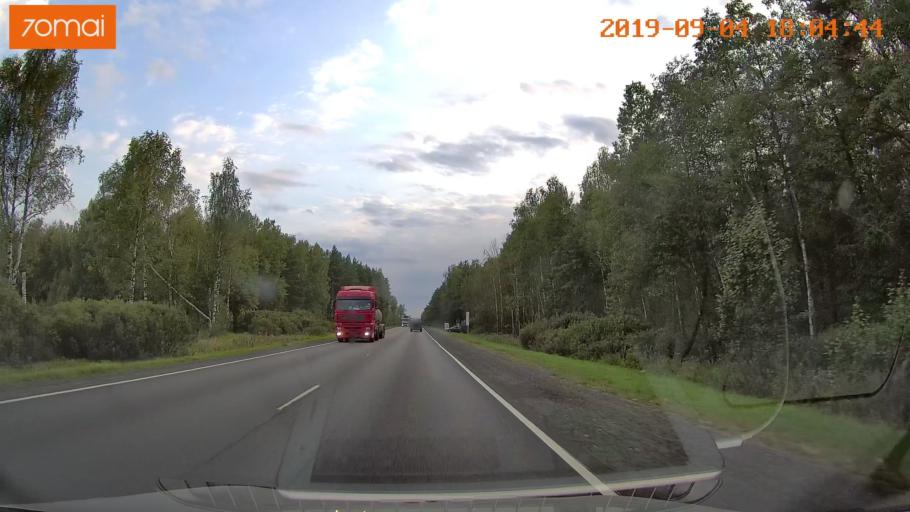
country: RU
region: Moskovskaya
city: Il'inskiy Pogost
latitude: 55.4489
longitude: 38.8352
